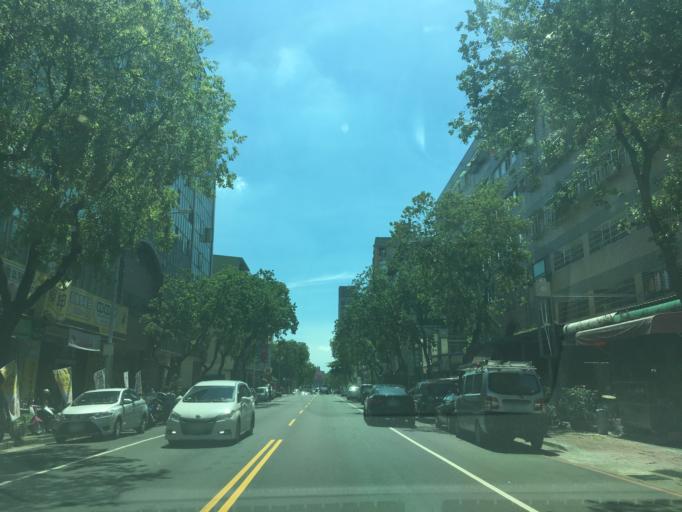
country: TW
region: Taiwan
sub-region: Taichung City
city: Taichung
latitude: 24.1427
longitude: 120.7059
